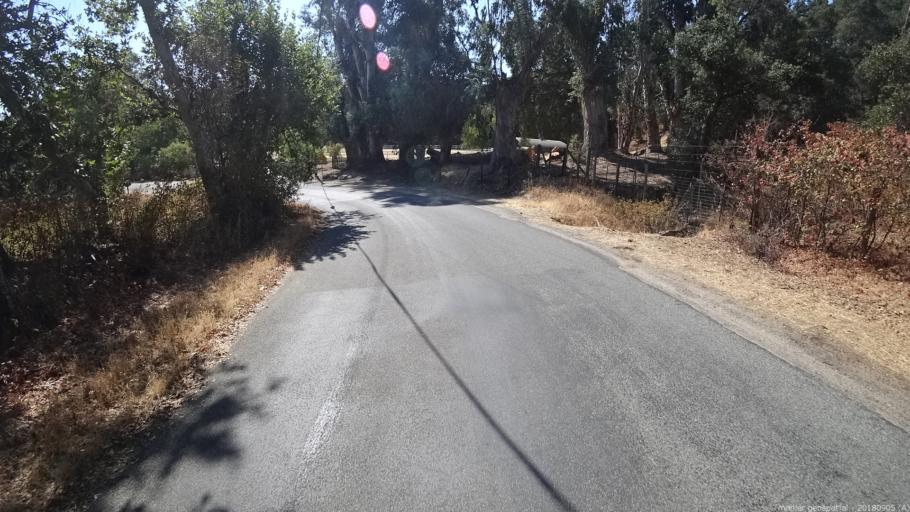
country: US
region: California
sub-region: Monterey County
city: Carmel Valley Village
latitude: 36.3923
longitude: -121.6394
